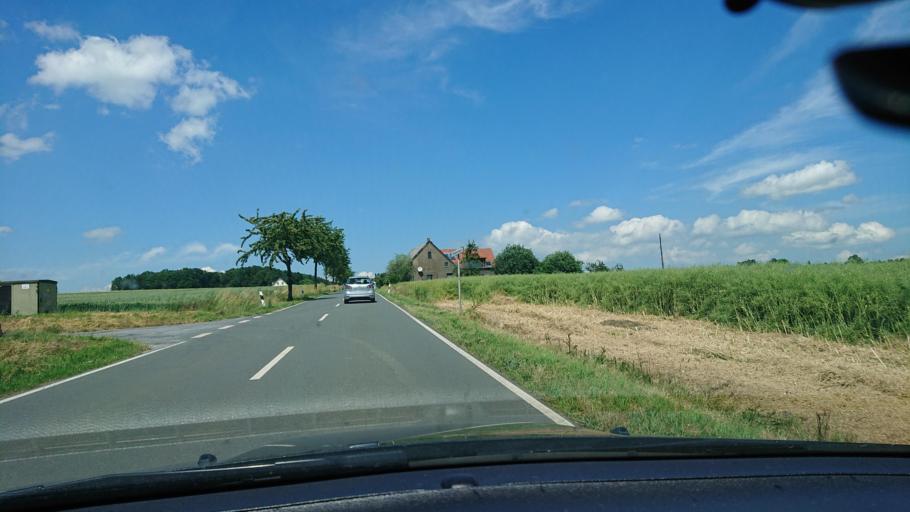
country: DE
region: North Rhine-Westphalia
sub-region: Regierungsbezirk Detmold
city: Rodinghausen
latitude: 52.2799
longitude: 8.4618
